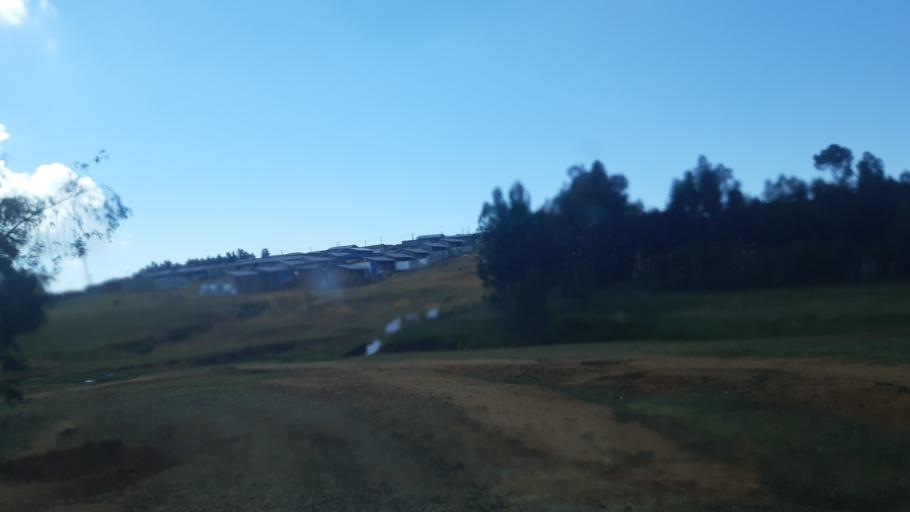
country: ET
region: Amhara
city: Dabat
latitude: 13.3569
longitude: 37.3849
